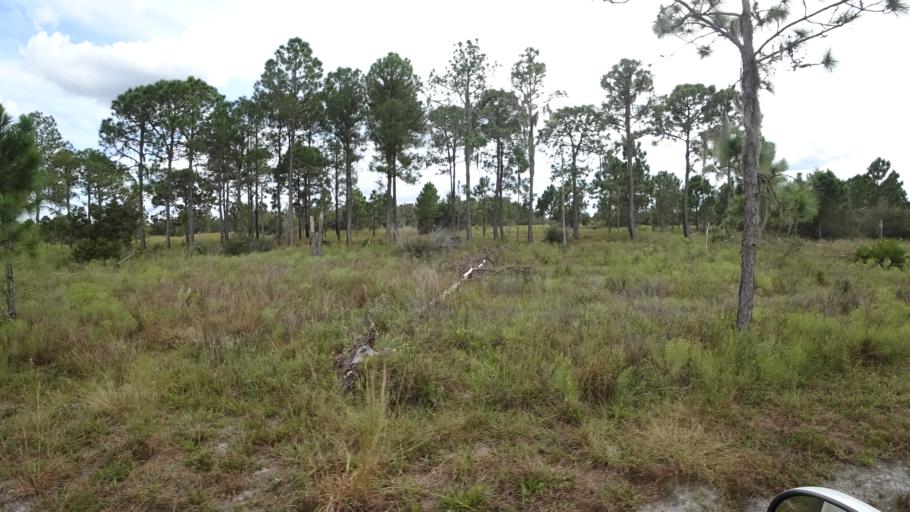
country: US
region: Florida
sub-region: Hillsborough County
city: Wimauma
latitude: 27.5538
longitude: -82.1368
